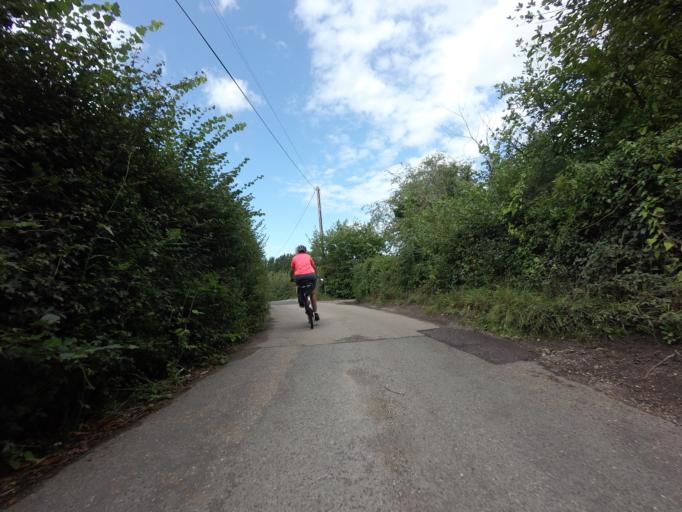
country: GB
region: England
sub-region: Kent
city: Shoreham
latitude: 51.3060
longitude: 0.1796
